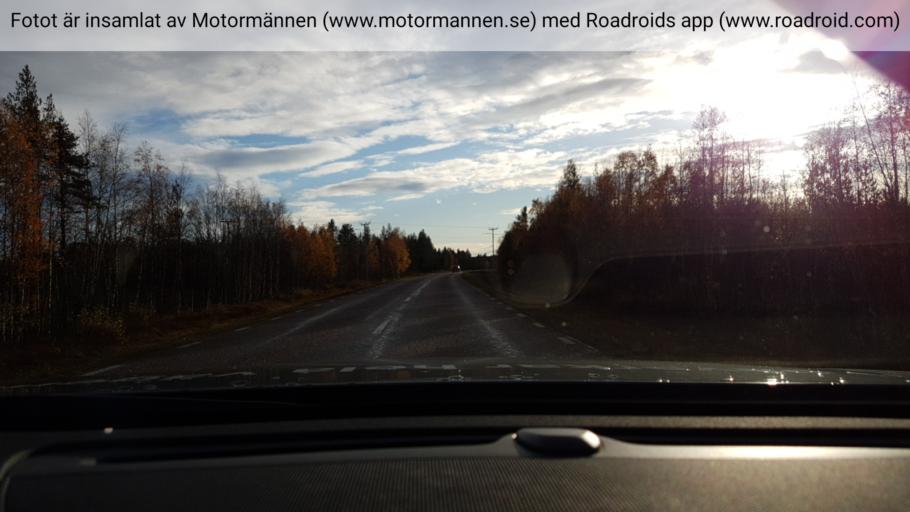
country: SE
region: Norrbotten
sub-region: Pajala Kommun
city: Pajala
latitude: 67.1775
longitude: 22.6966
